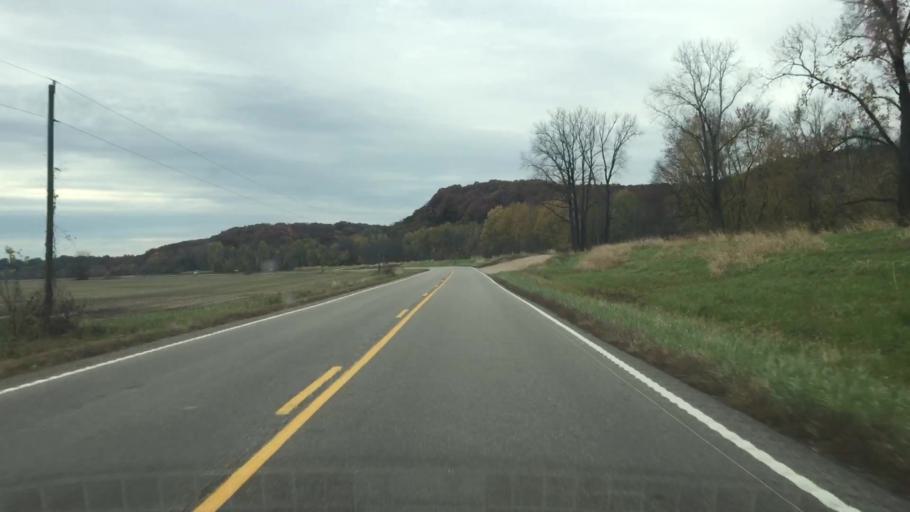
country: US
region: Missouri
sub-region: Callaway County
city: Fulton
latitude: 38.7067
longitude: -91.7806
